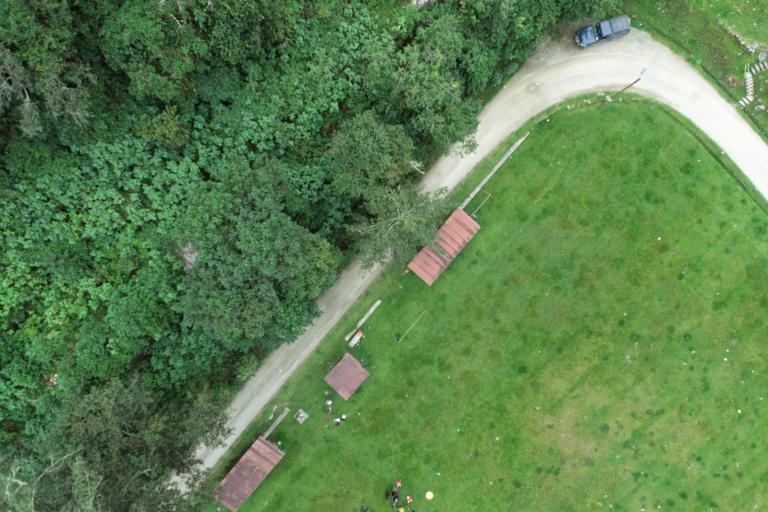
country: BO
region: La Paz
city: Coroico
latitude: -16.1233
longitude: -68.0890
